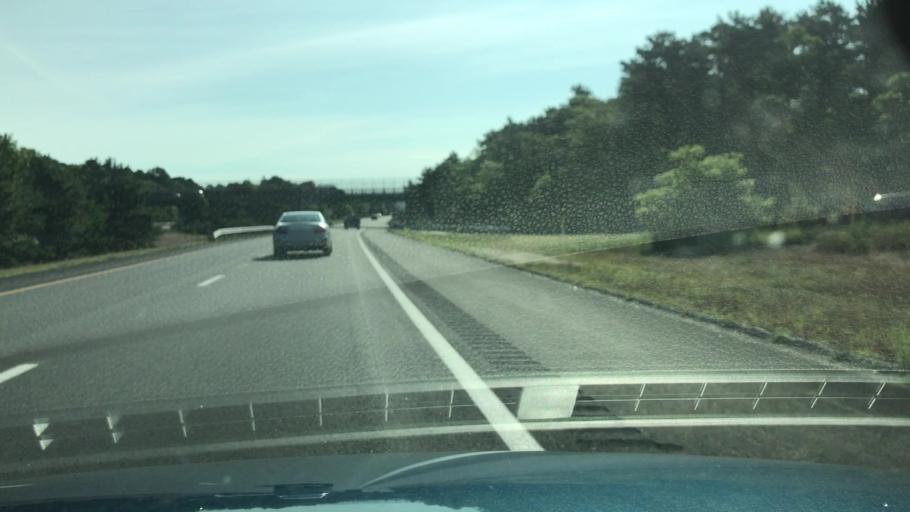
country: US
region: Massachusetts
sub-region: Barnstable County
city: South Dennis
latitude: 41.6973
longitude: -70.1557
